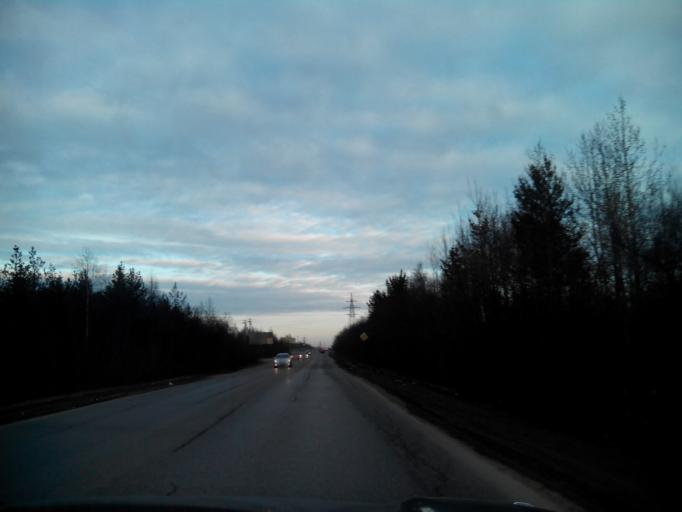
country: RU
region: Arkhangelskaya
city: Arkhangel'sk
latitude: 64.5219
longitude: 40.6710
